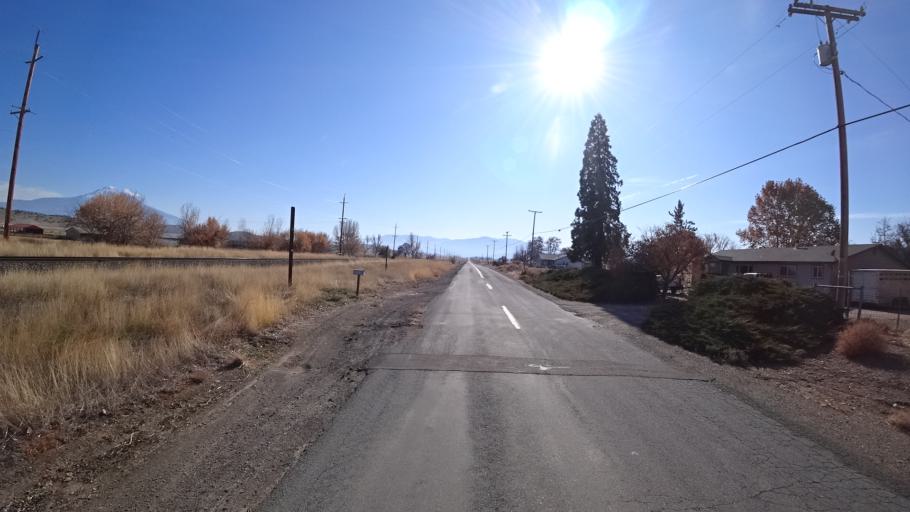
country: US
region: California
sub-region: Siskiyou County
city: Montague
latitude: 41.6196
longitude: -122.5226
